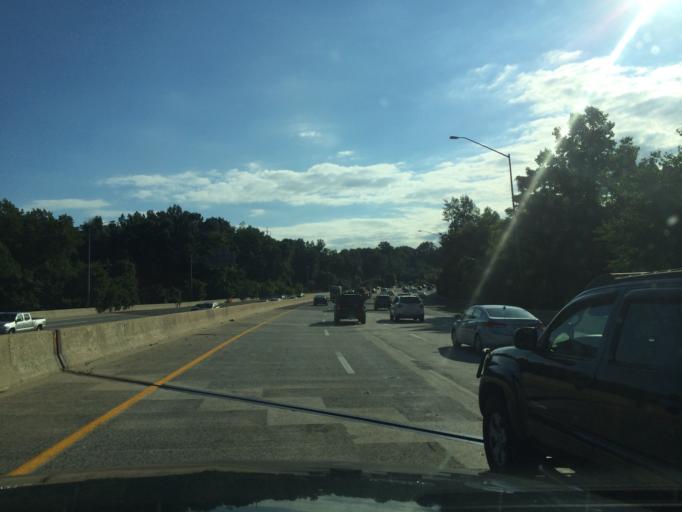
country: US
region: Maryland
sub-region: Montgomery County
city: Cabin John
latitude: 38.9851
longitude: -77.1586
